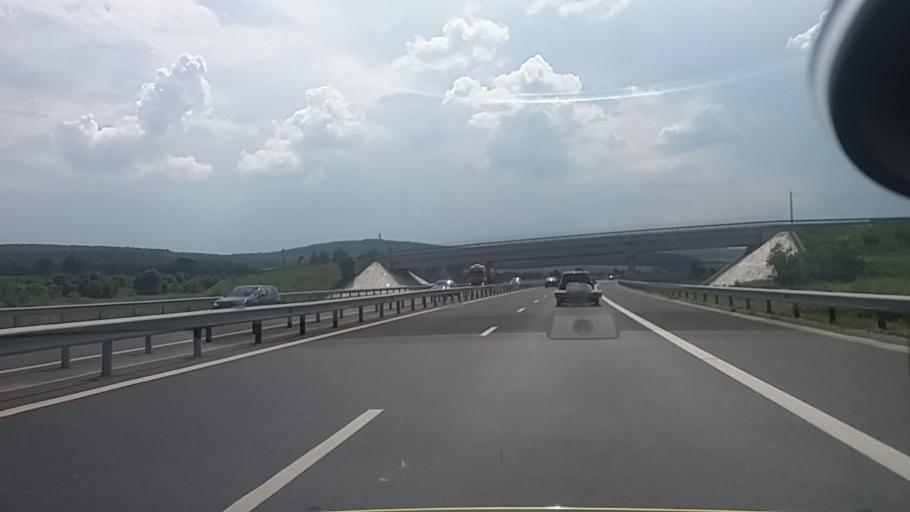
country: RO
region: Hunedoara
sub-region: Comuna Turdas
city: Turdas
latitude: 45.8406
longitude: 23.1219
